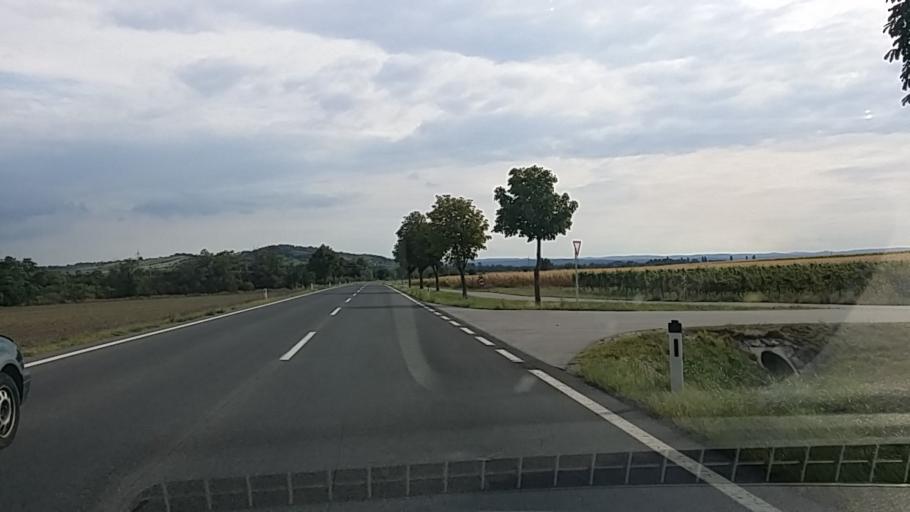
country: AT
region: Burgenland
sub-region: Eisenstadt-Umgebung
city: Schutzen am Gebirge
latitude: 47.8655
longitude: 16.6462
